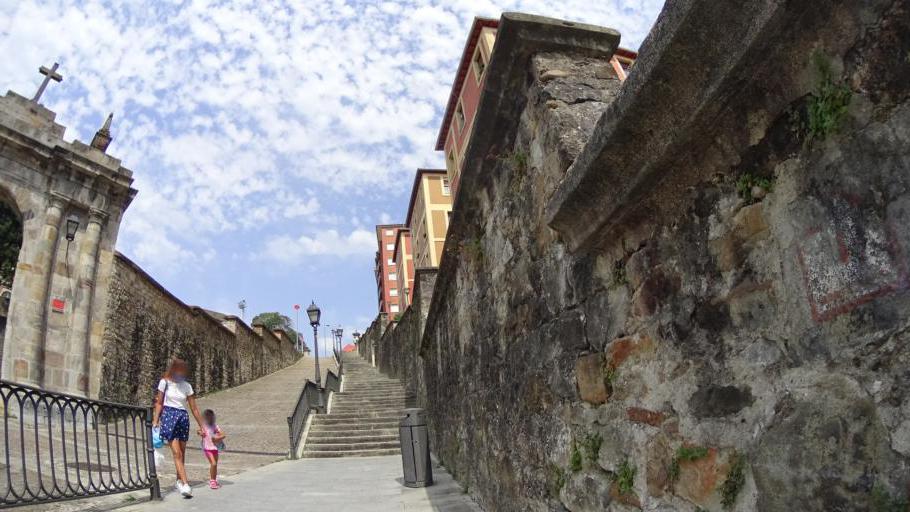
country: ES
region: Basque Country
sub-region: Bizkaia
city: Bilbao
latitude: 43.2598
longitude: -2.9201
